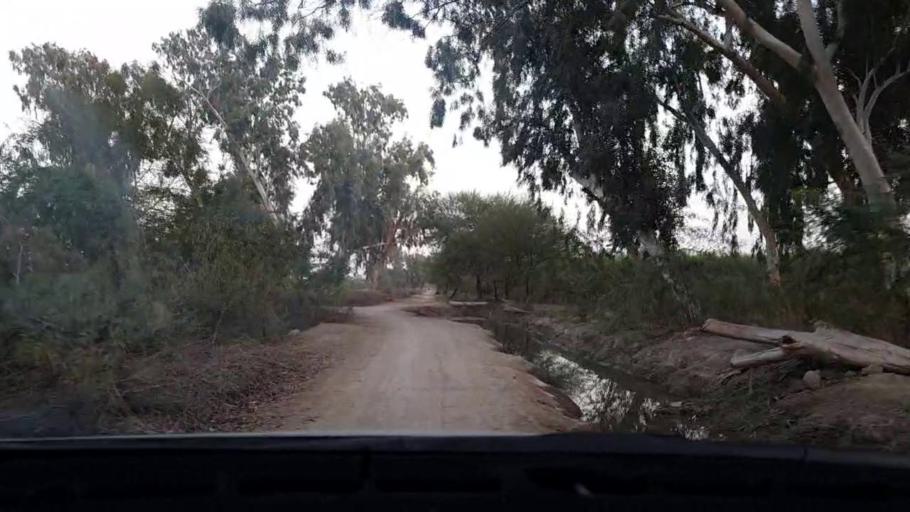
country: PK
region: Sindh
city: Tando Mittha Khan
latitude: 25.8630
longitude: 69.3186
